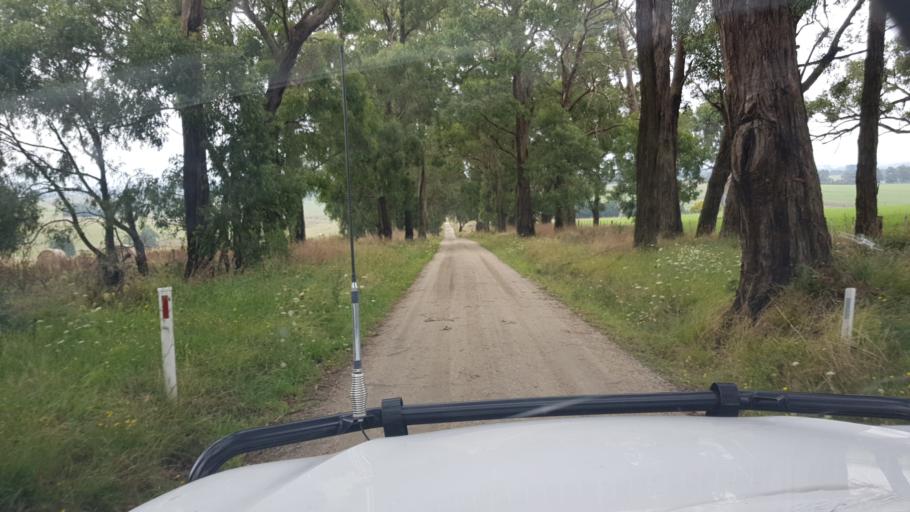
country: AU
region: Victoria
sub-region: Baw Baw
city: Warragul
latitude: -38.1043
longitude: 145.9965
